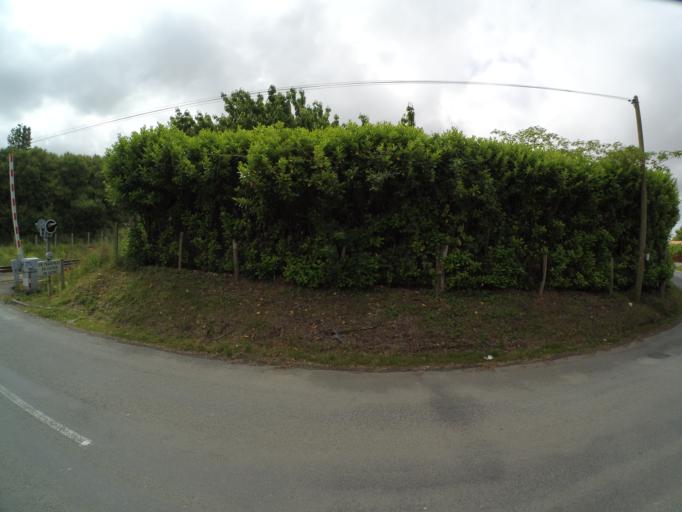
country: FR
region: Poitou-Charentes
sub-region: Departement de la Charente-Maritime
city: Yves
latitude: 46.0207
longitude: -1.0463
